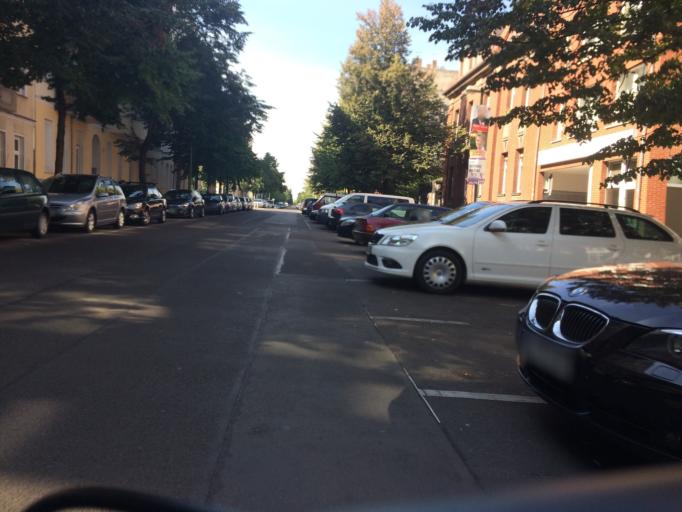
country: DE
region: Berlin
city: Prenzlauer Berg Bezirk
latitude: 52.5443
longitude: 13.4390
